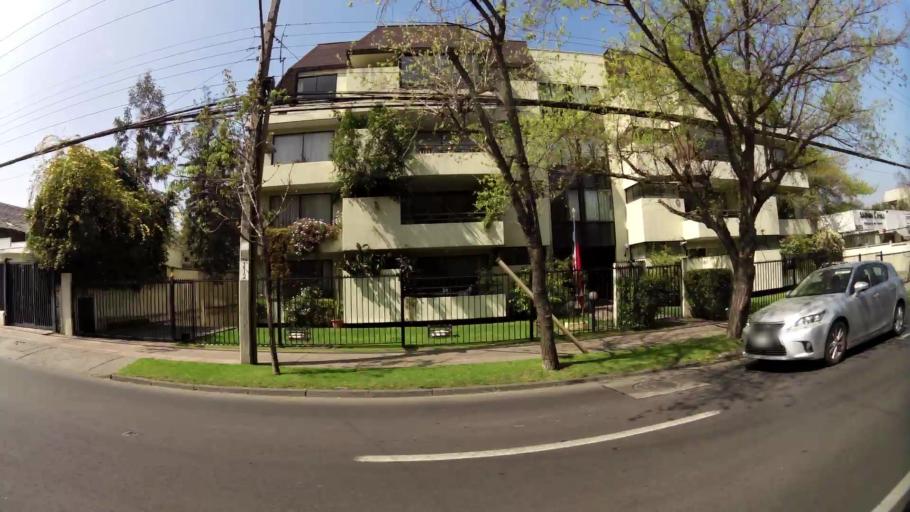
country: CL
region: Santiago Metropolitan
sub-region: Provincia de Santiago
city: Villa Presidente Frei, Nunoa, Santiago, Chile
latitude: -33.3908
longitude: -70.5794
